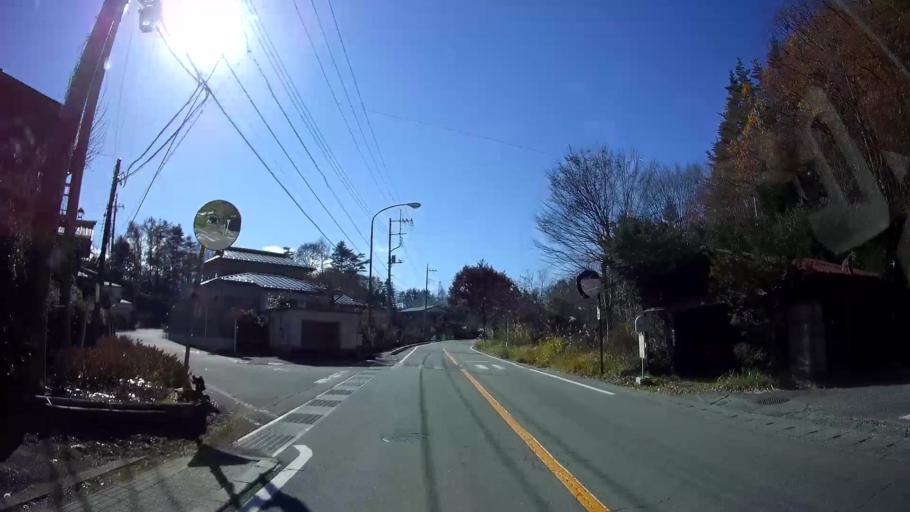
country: JP
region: Yamanashi
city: Fujikawaguchiko
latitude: 35.4948
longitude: 138.7310
